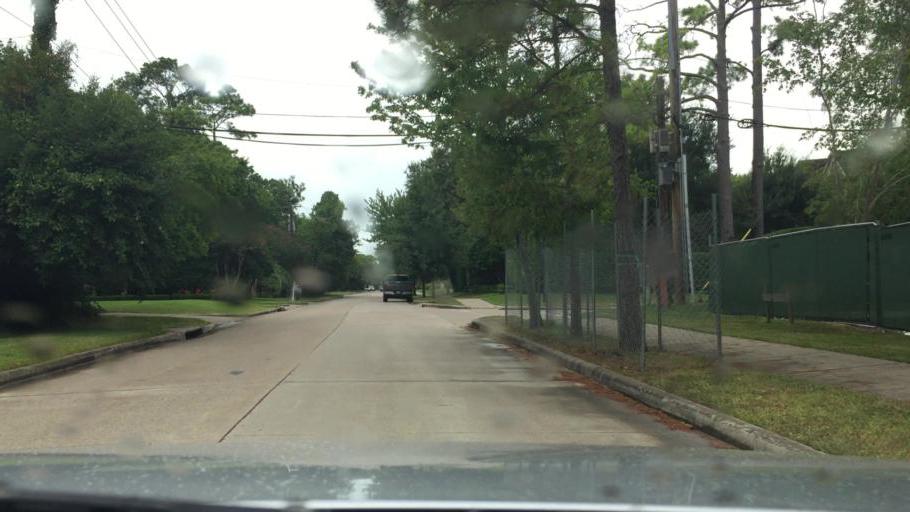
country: US
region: Texas
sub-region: Harris County
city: Piney Point Village
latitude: 29.7667
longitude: -95.5088
